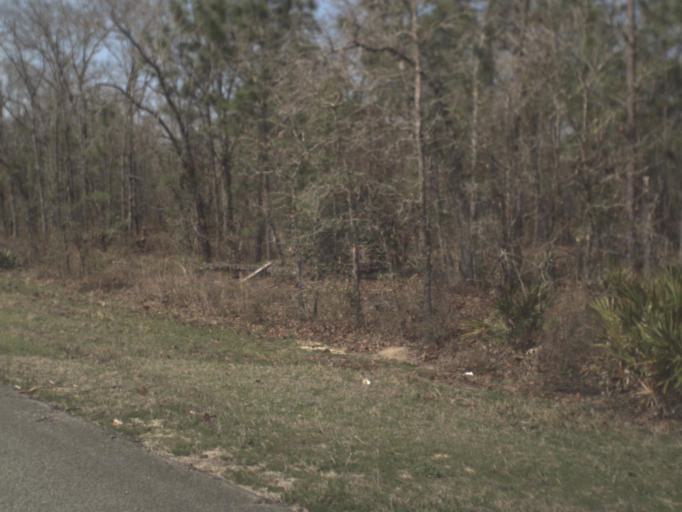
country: US
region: Florida
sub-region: Liberty County
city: Bristol
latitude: 30.5056
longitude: -84.8443
